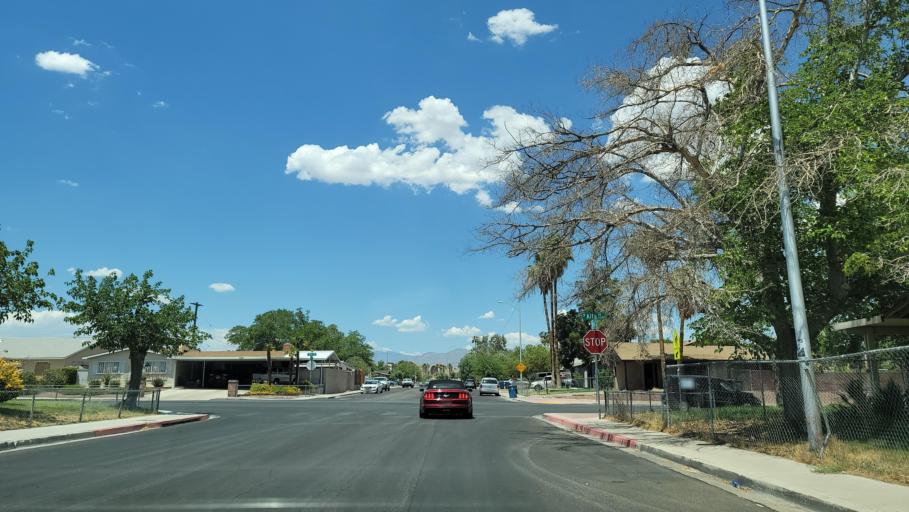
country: US
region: Nevada
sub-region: Clark County
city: Las Vegas
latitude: 36.1664
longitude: -115.1973
